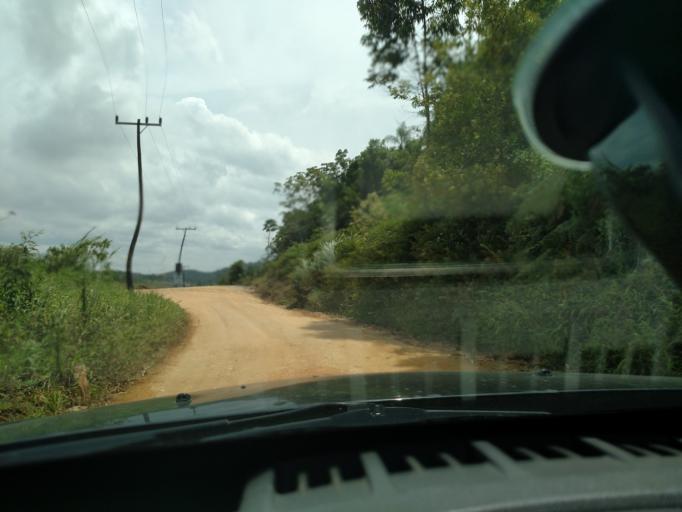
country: BR
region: Santa Catarina
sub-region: Itajai
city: Itajai
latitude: -26.9661
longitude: -48.7993
